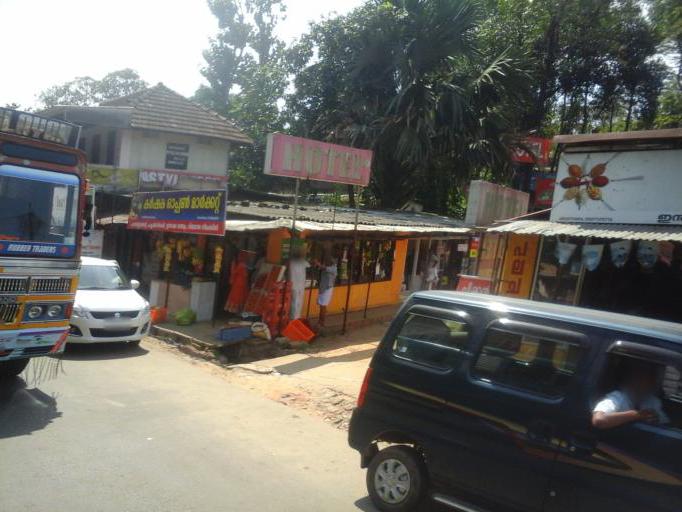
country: IN
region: Kerala
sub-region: Kottayam
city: Erattupetta
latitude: 9.6851
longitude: 76.7774
